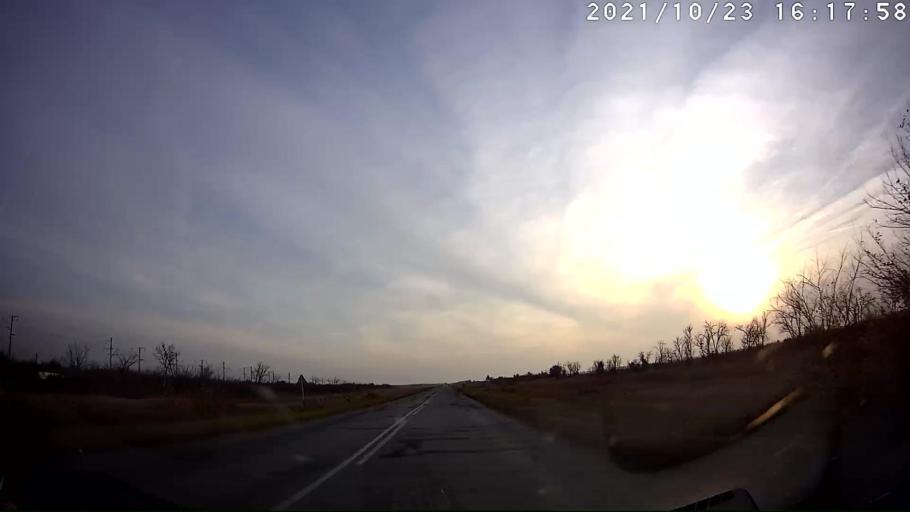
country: RU
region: Volgograd
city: Kotel'nikovo
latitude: 47.9069
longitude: 43.5528
